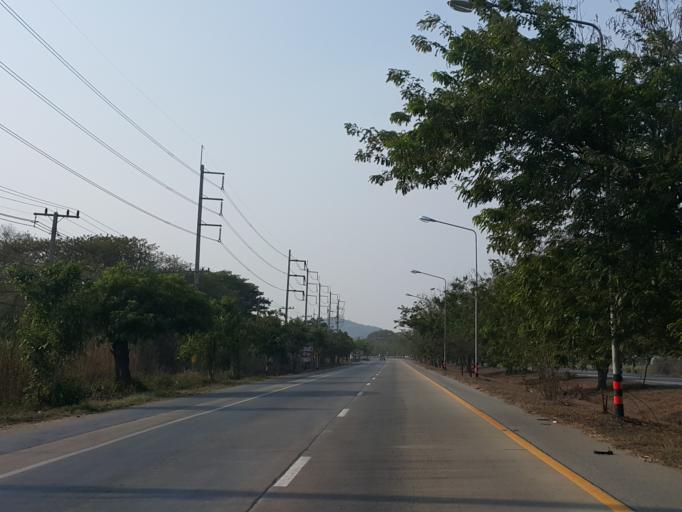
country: TH
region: Suphan Buri
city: Doembang Nangbuat
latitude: 14.8267
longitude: 100.1144
